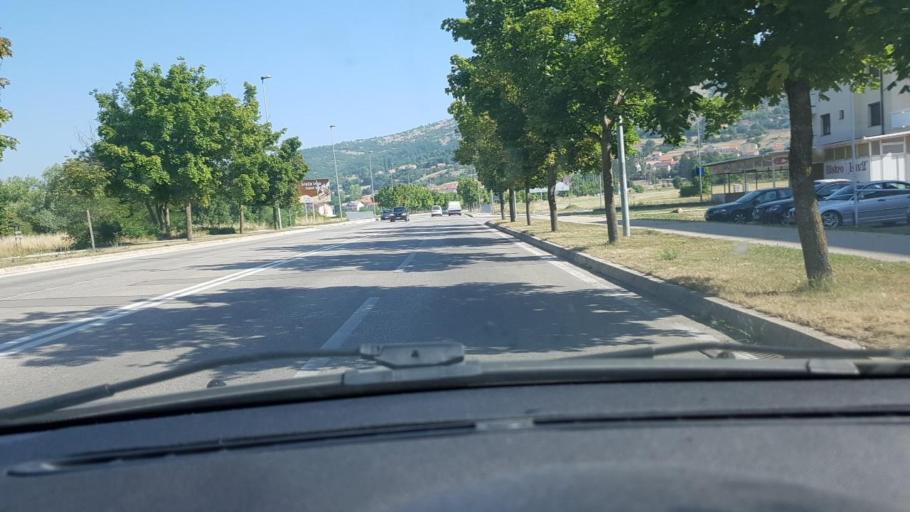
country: BA
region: Federation of Bosnia and Herzegovina
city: Livno
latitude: 43.8243
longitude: 16.9969
